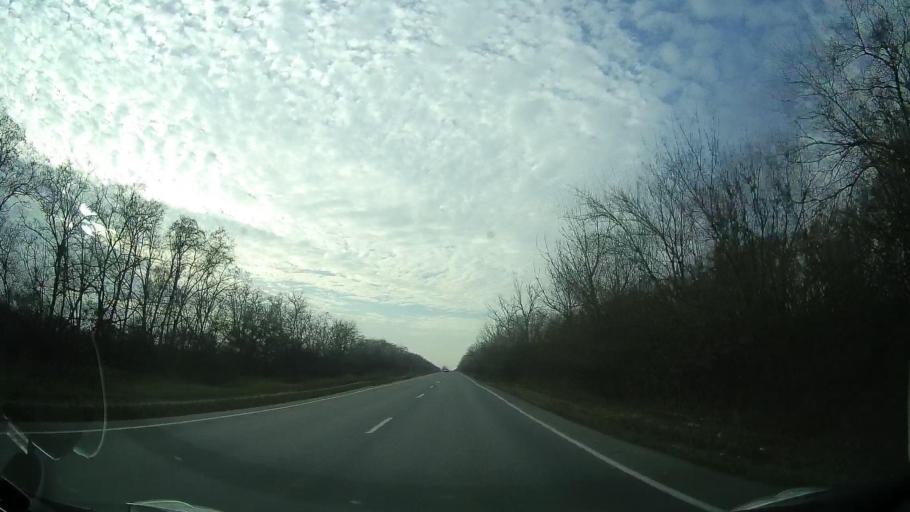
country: RU
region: Rostov
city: Bagayevskaya
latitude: 47.0960
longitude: 40.2935
